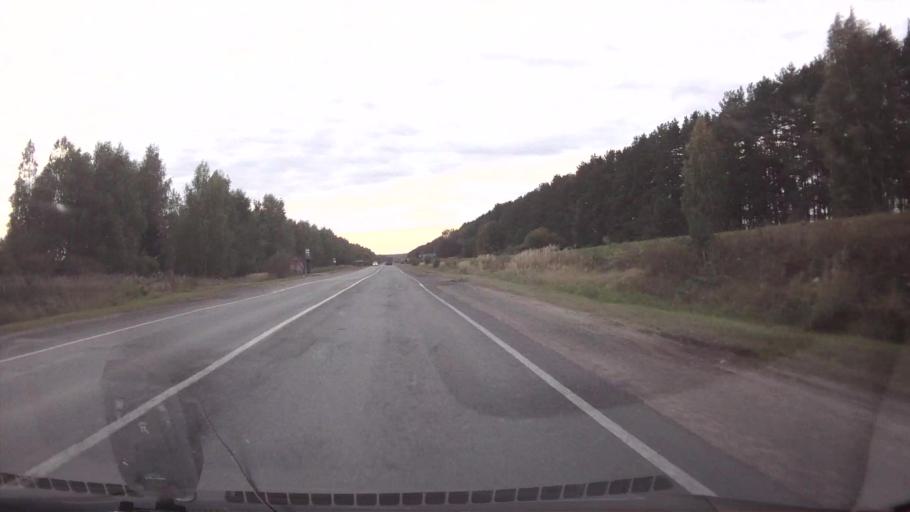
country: RU
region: Mariy-El
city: Sovetskiy
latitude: 56.7459
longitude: 48.2870
